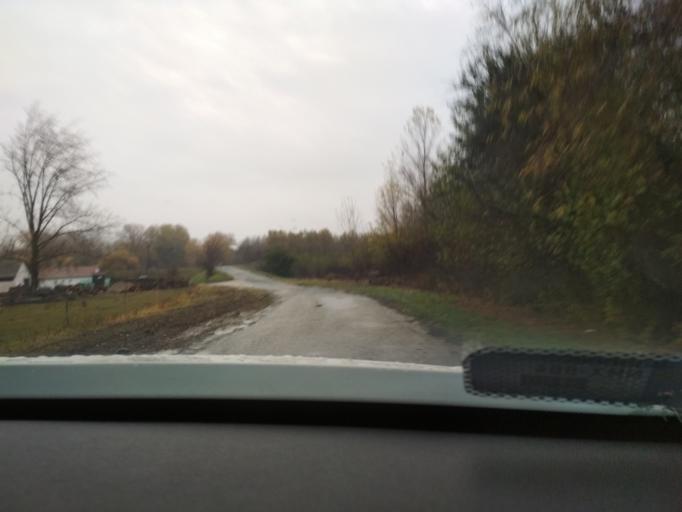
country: HU
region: Csongrad
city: Mindszent
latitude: 46.5366
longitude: 20.1530
